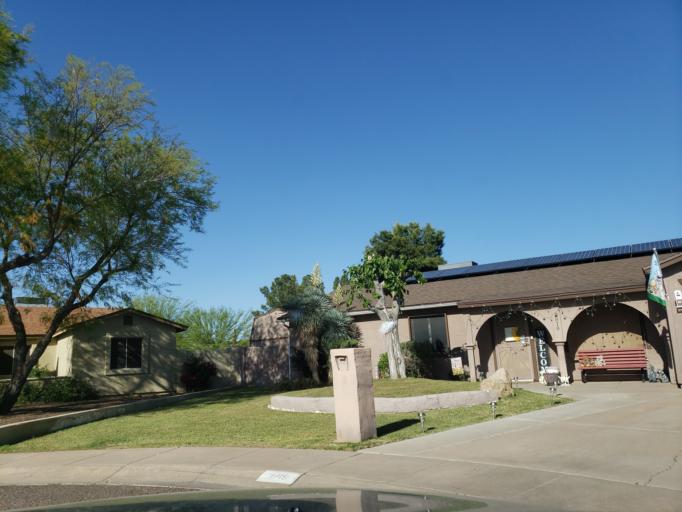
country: US
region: Arizona
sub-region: Maricopa County
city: Paradise Valley
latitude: 33.6220
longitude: -111.9997
